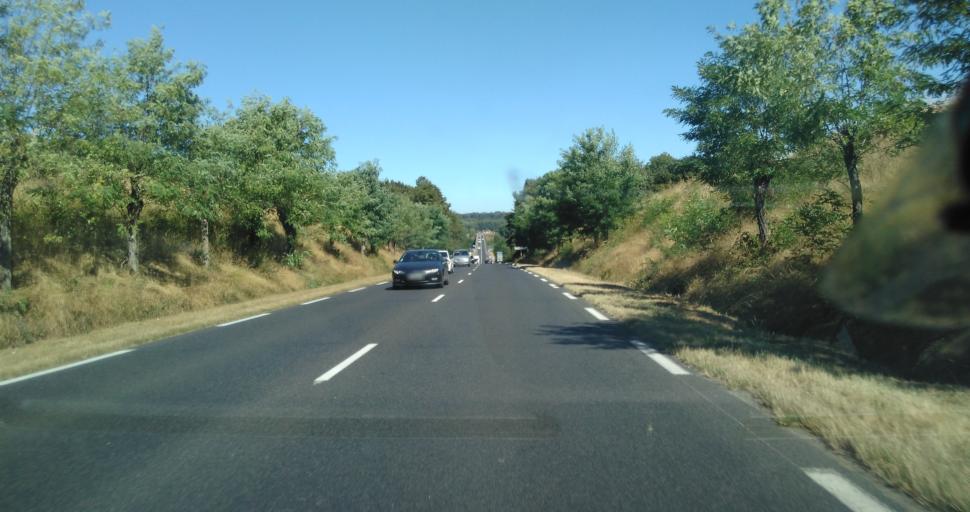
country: FR
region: Centre
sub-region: Departement d'Indre-et-Loire
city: Charge
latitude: 47.4199
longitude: 1.0151
